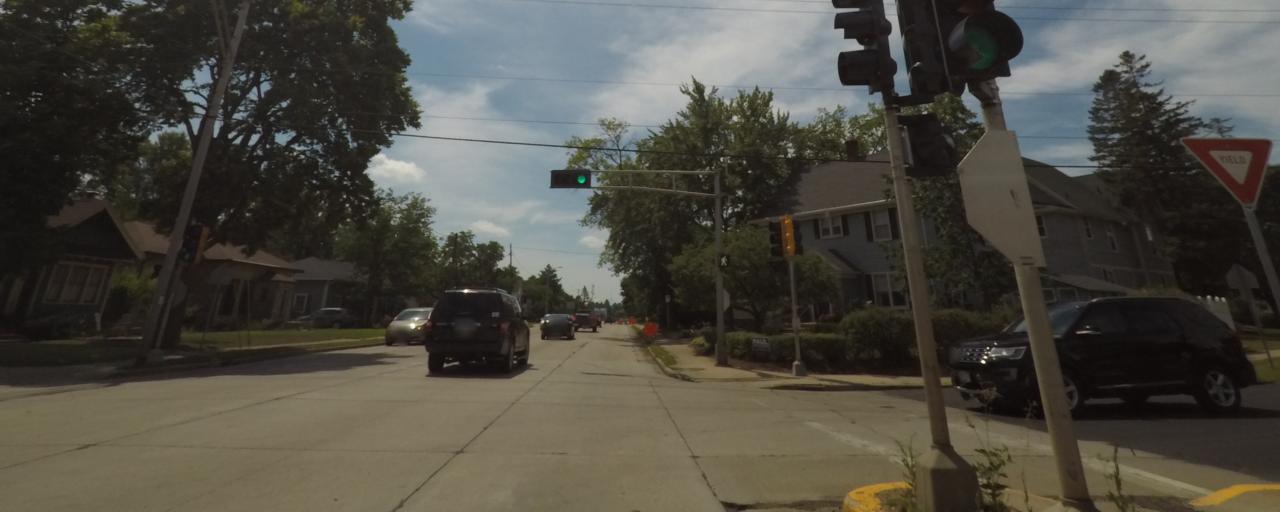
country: US
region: Wisconsin
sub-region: Portage County
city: Stevens Point
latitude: 44.5195
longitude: -89.5748
